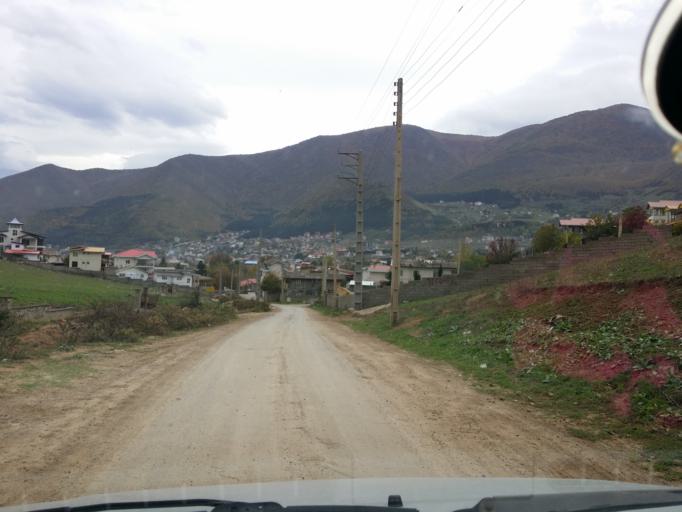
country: IR
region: Mazandaran
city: `Abbasabad
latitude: 36.5064
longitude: 51.1438
